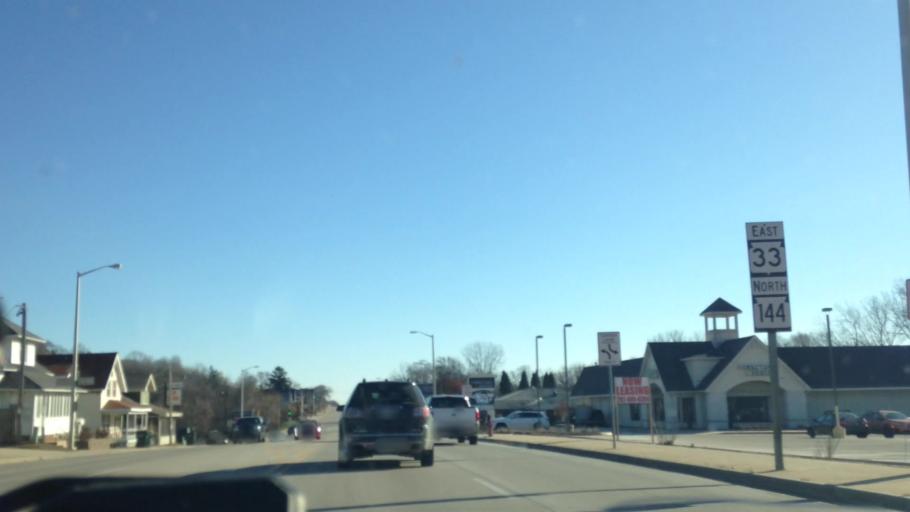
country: US
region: Wisconsin
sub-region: Washington County
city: West Bend
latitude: 43.4270
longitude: -88.1966
